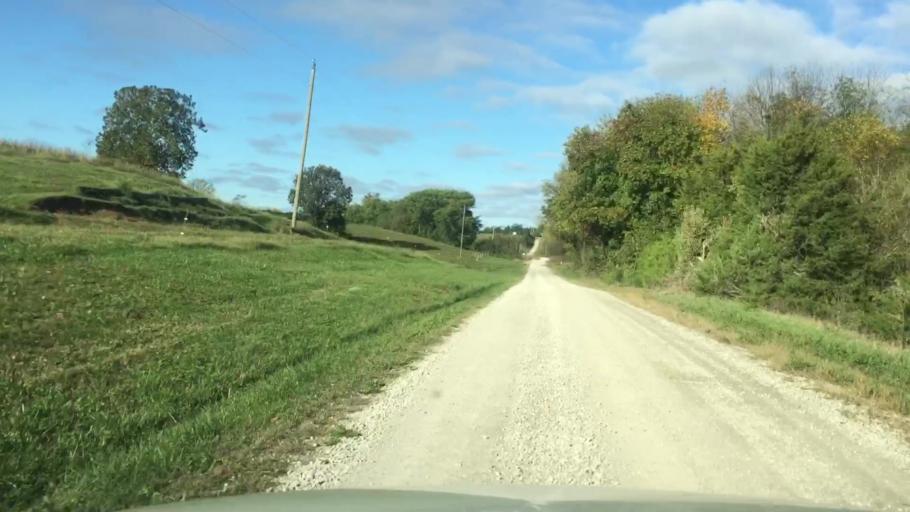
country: US
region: Missouri
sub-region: Howard County
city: New Franklin
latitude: 39.0832
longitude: -92.7627
